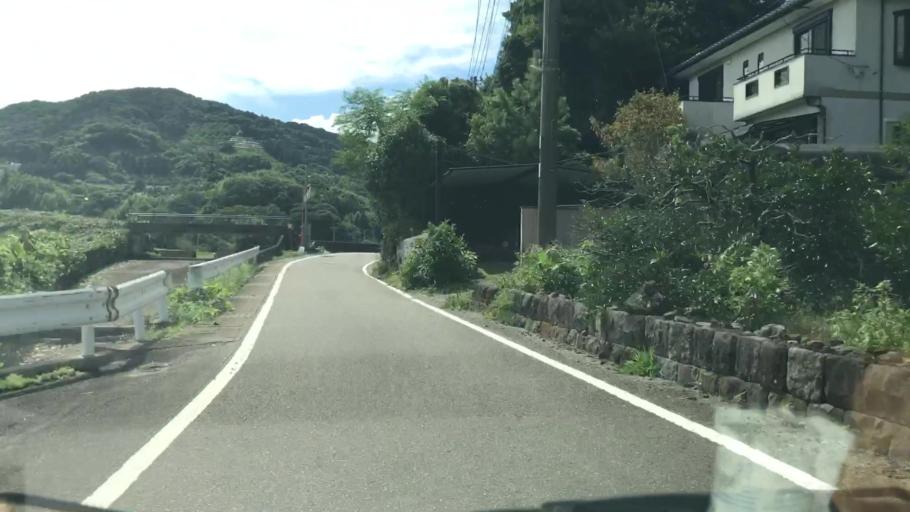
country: JP
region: Saga Prefecture
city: Saga-shi
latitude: 33.2343
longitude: 130.1751
